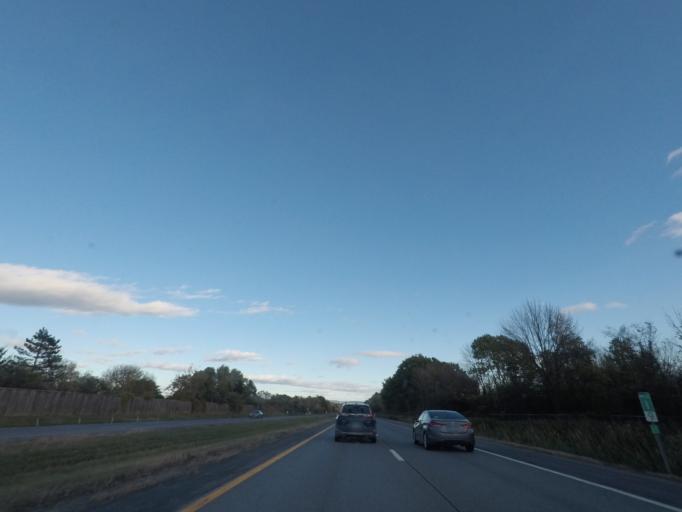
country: US
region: New York
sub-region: Albany County
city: Cohoes
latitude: 42.7545
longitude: -73.7285
